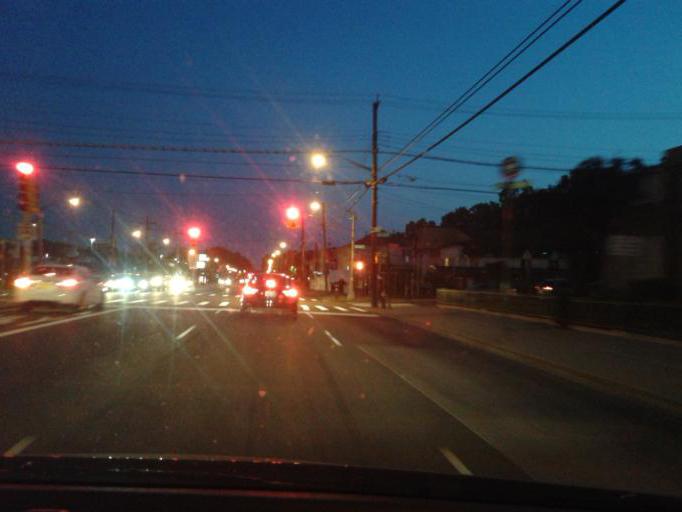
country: US
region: New York
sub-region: Richmond County
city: Staten Island
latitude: 40.5669
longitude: -74.1135
